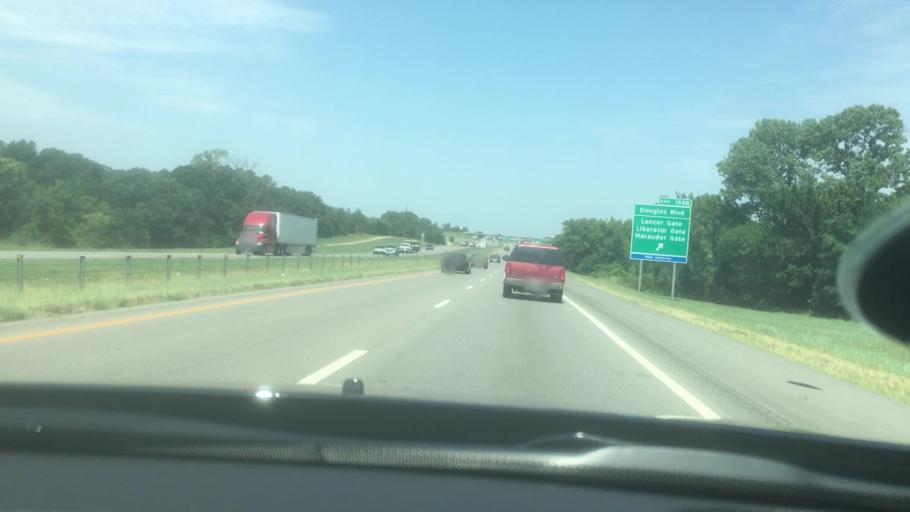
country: US
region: Oklahoma
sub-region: Oklahoma County
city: Midwest City
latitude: 35.4289
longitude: -97.3614
